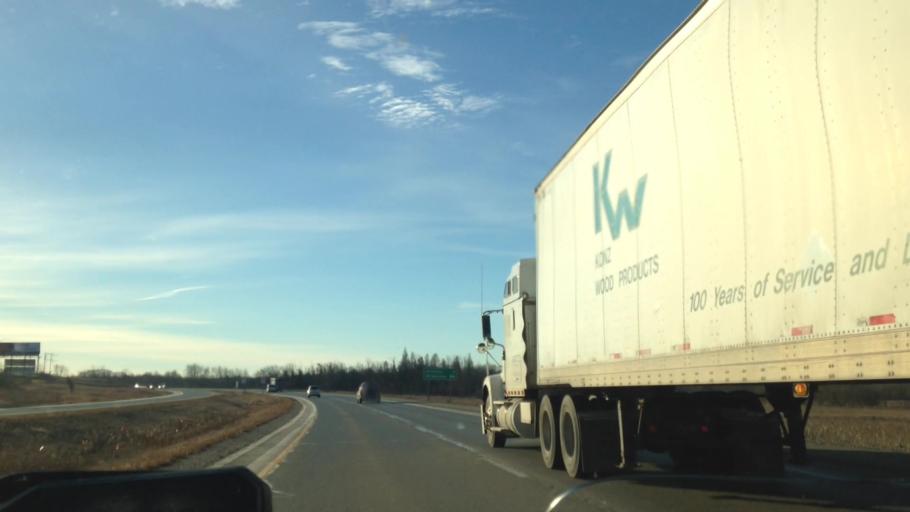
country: US
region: Wisconsin
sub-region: Dodge County
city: Theresa
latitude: 43.4622
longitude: -88.3667
